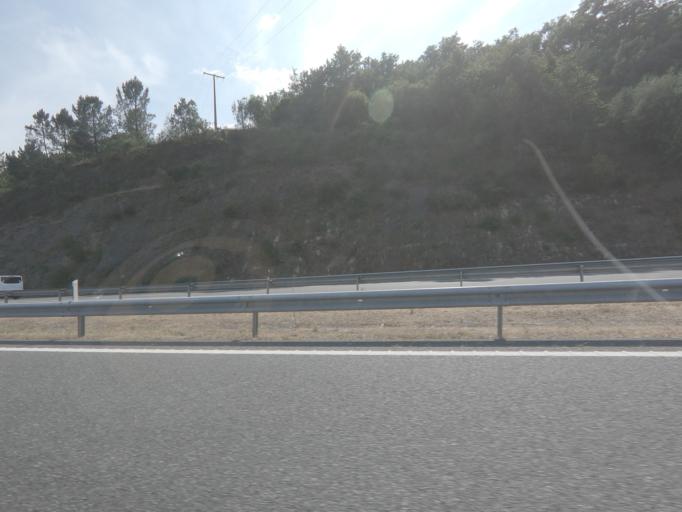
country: ES
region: Galicia
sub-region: Provincia de Ourense
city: Cenlle
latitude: 42.3229
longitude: -8.0764
